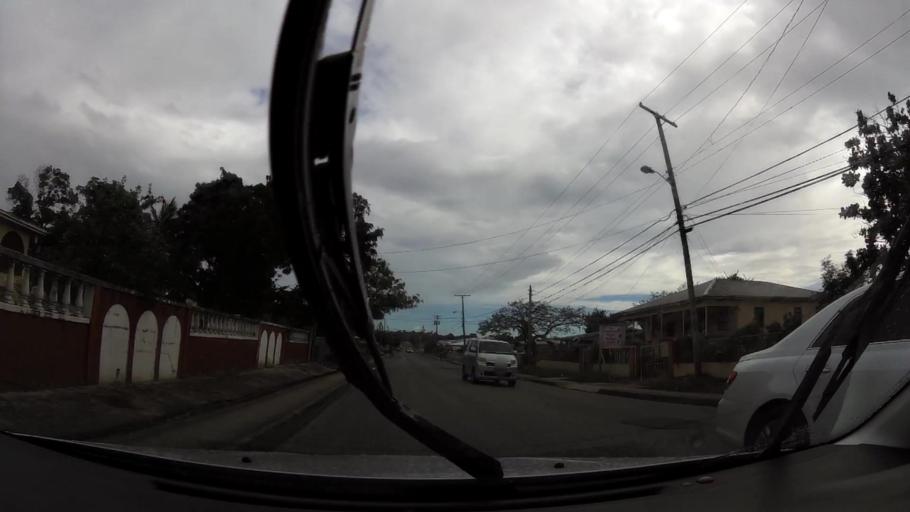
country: AG
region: Saint John
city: Saint John's
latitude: 17.1055
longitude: -61.8331
